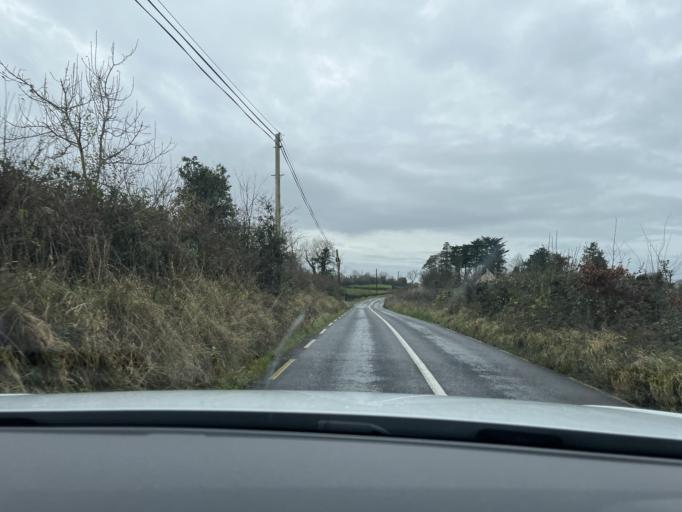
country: IE
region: Connaught
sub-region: County Leitrim
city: Manorhamilton
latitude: 54.2485
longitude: -8.2510
